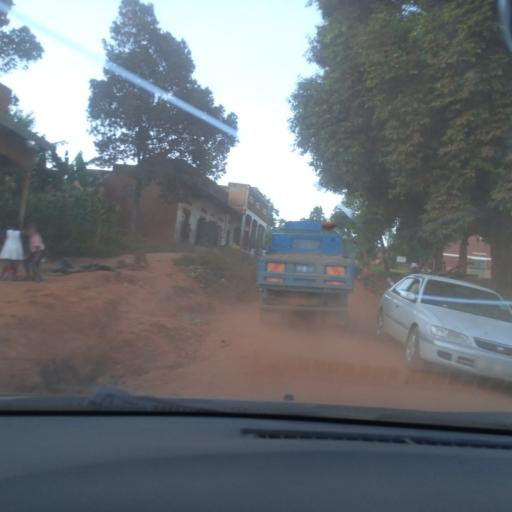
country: UG
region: Central Region
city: Masaka
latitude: -0.3155
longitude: 31.7705
